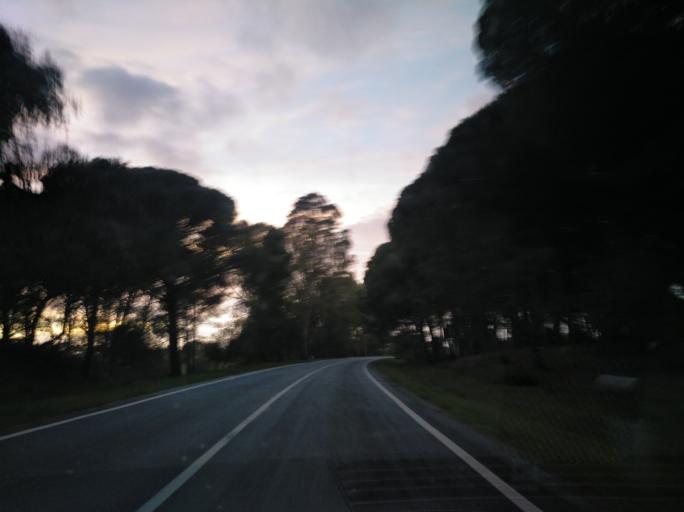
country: PT
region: Setubal
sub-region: Grandola
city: Grandola
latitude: 38.2010
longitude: -8.6220
